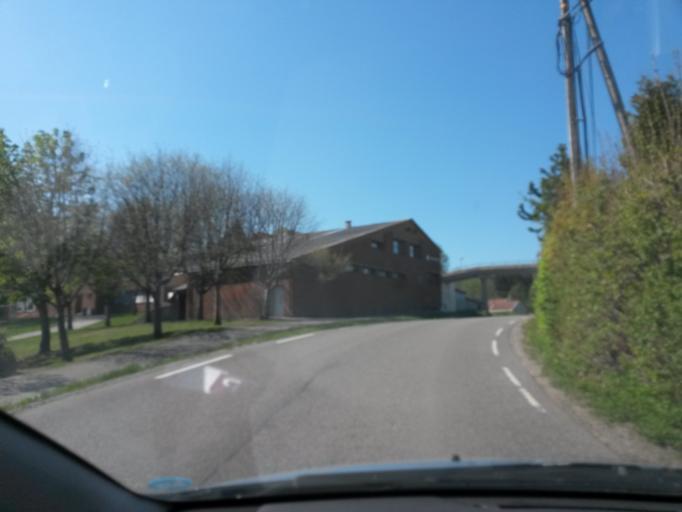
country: NO
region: Akershus
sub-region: Asker
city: Asker
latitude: 59.8292
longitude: 10.4045
